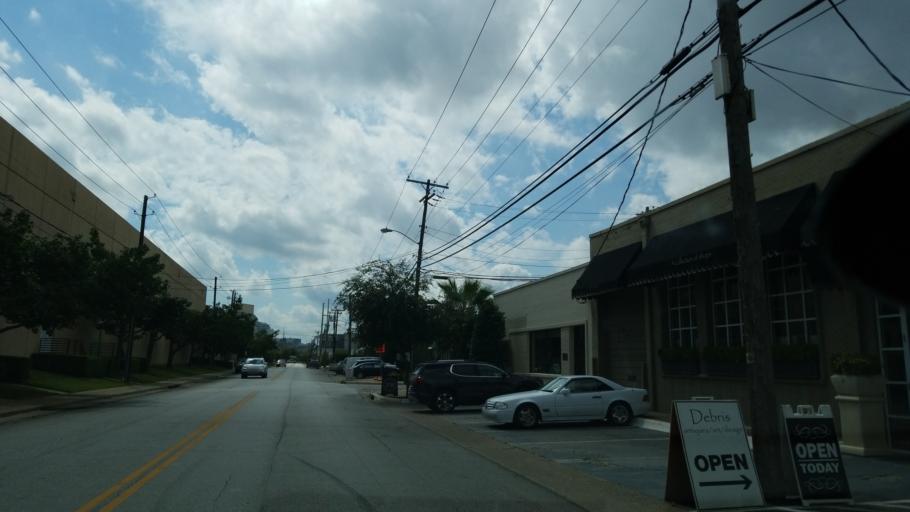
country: US
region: Texas
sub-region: Dallas County
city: Dallas
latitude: 32.7898
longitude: -96.8165
